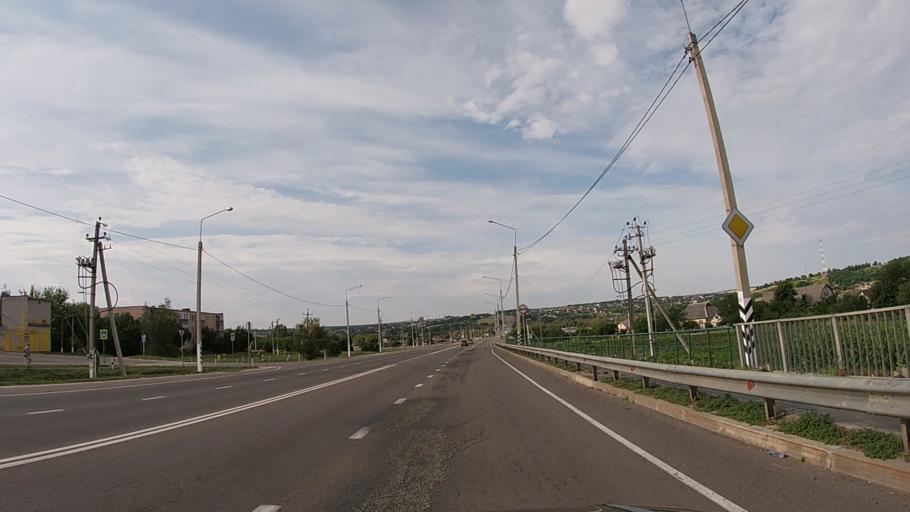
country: RU
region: Belgorod
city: Severnyy
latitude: 50.6403
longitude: 36.4684
